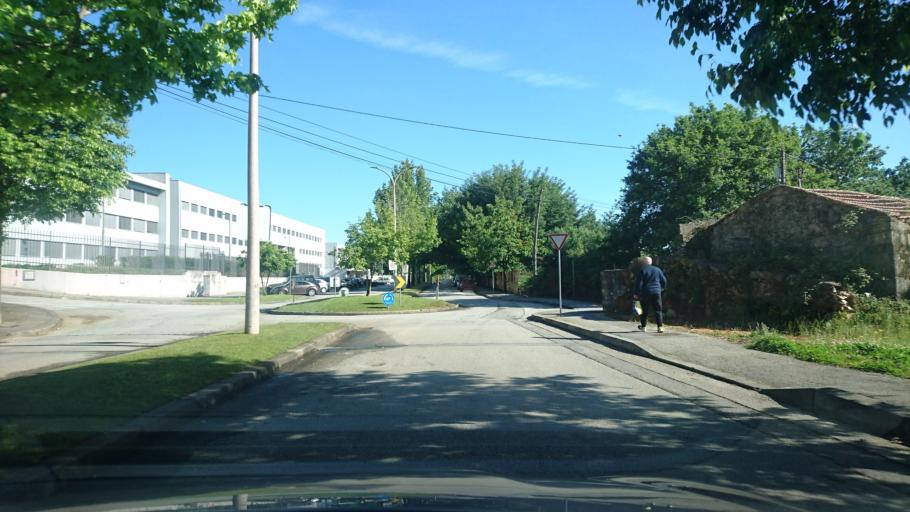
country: PT
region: Aveiro
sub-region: Sao Joao da Madeira
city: Sao Joao da Madeira
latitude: 40.8915
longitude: -8.4847
